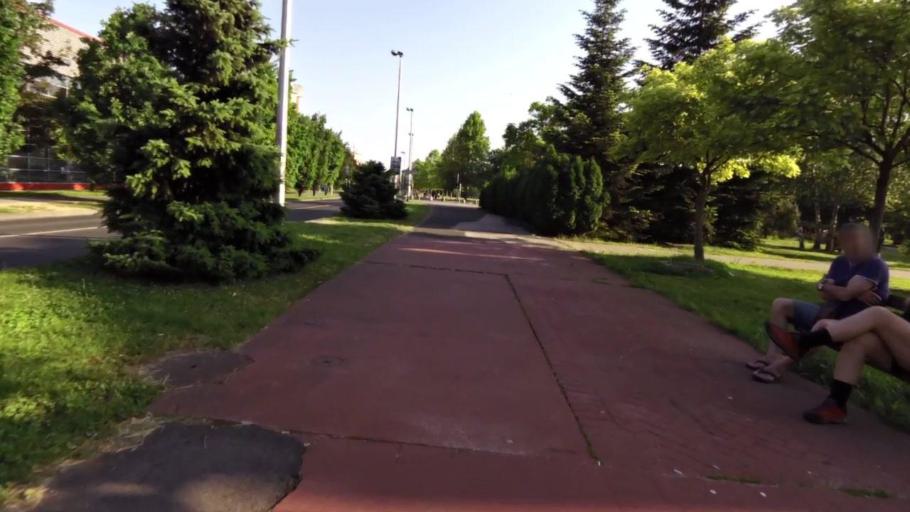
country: HR
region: Grad Zagreb
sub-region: Sesvete
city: Sesvete
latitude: 45.8331
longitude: 16.1073
